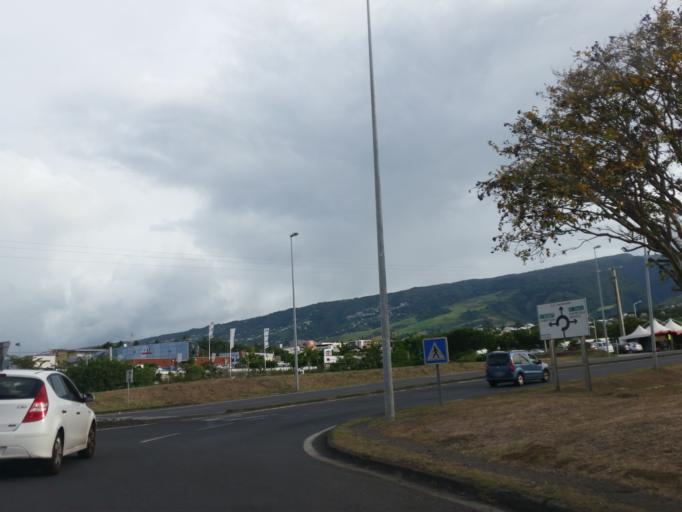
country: RE
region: Reunion
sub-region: Reunion
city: Saint-Denis
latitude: -20.8997
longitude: 55.4975
